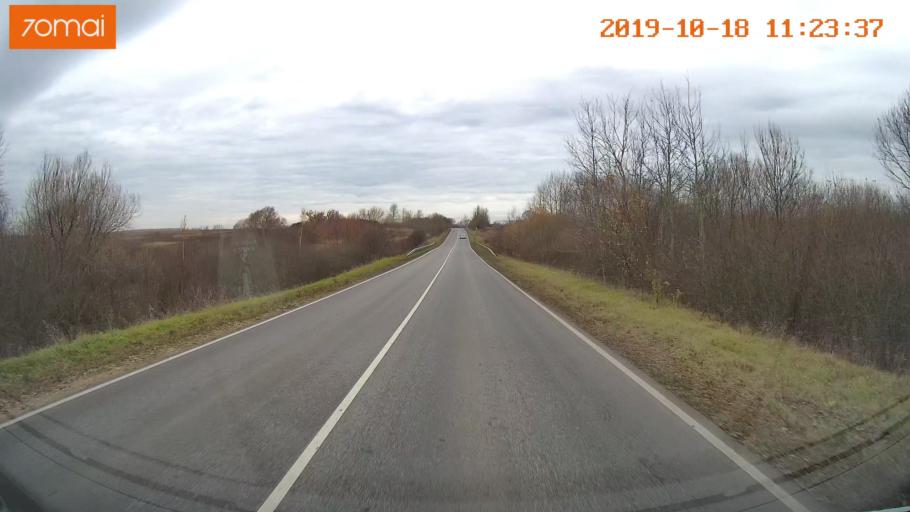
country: RU
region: Tula
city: Kimovsk
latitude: 54.1040
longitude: 38.5949
